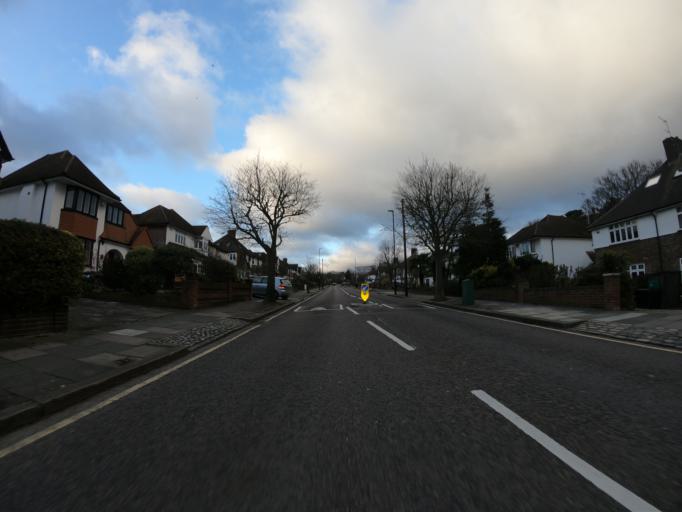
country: GB
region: England
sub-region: Greater London
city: Welling
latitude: 51.4536
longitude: 0.0781
